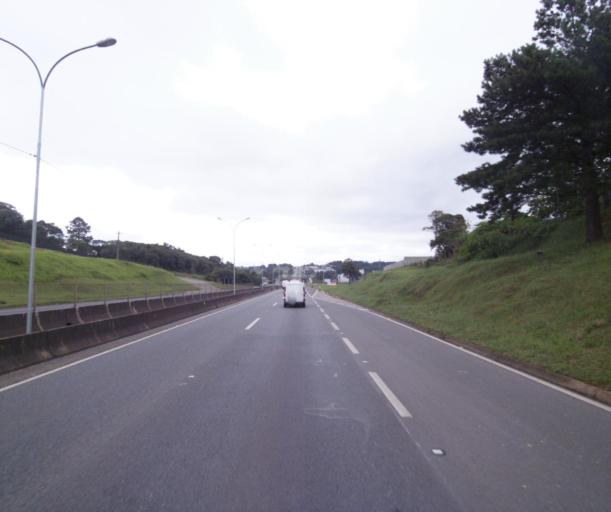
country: BR
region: Parana
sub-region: Quatro Barras
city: Quatro Barras
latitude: -25.3694
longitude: -49.1150
